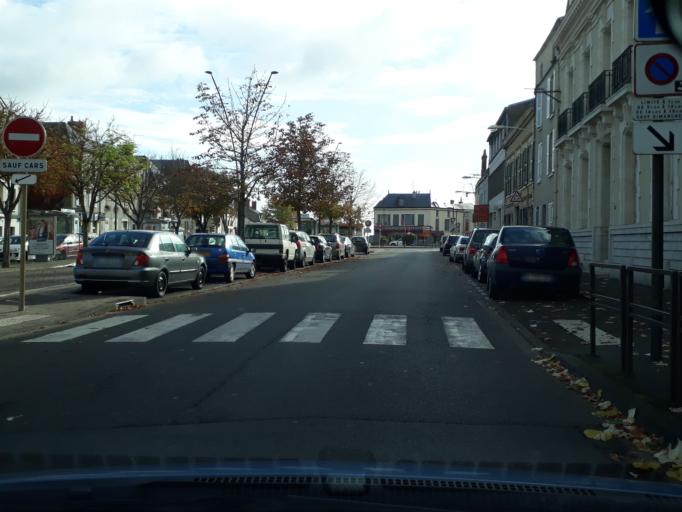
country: FR
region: Centre
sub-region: Departement du Loiret
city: Pithiviers
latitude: 48.1720
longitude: 2.2532
